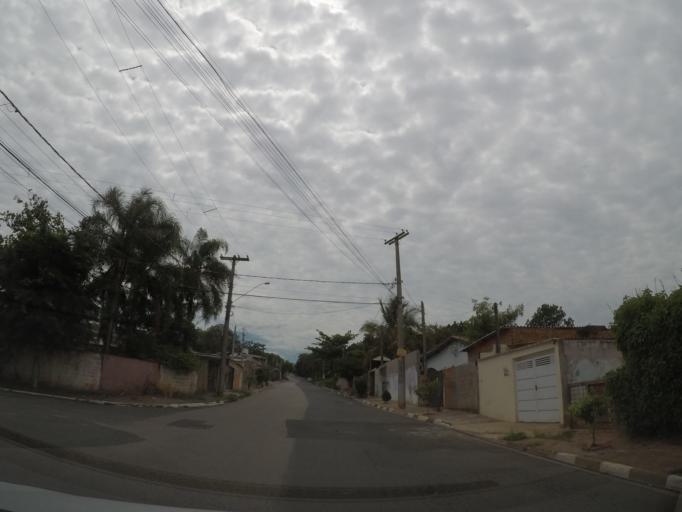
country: BR
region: Sao Paulo
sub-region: Hortolandia
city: Hortolandia
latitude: -22.8370
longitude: -47.2045
